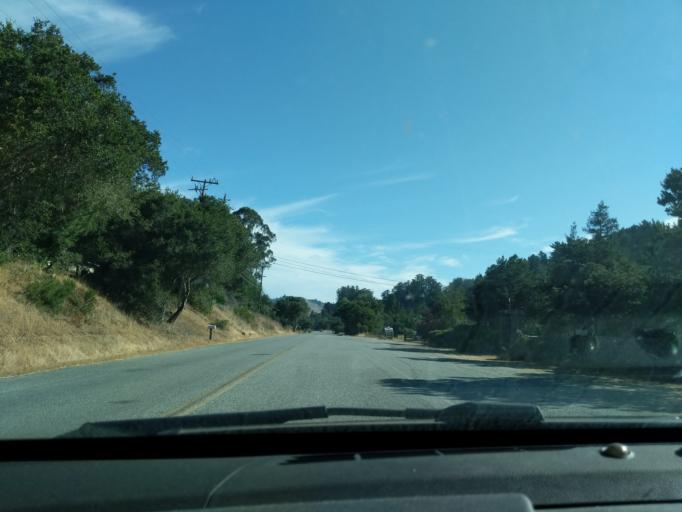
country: US
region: California
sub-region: San Benito County
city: Aromas
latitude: 36.8744
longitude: -121.6423
